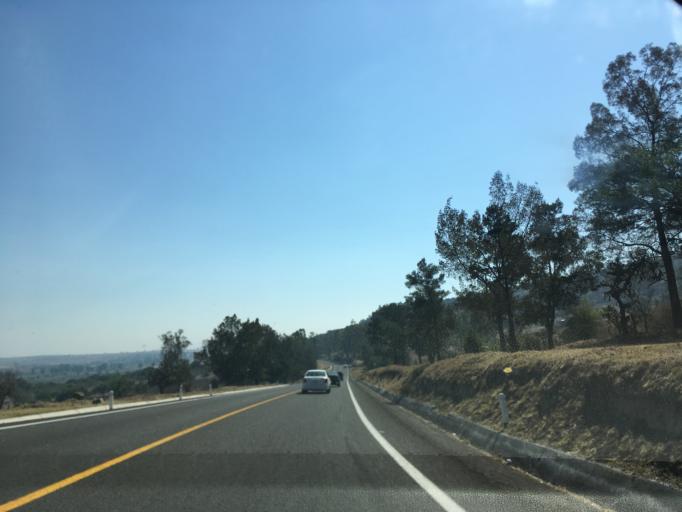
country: MX
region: Michoacan
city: Charo
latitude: 19.7754
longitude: -101.0153
